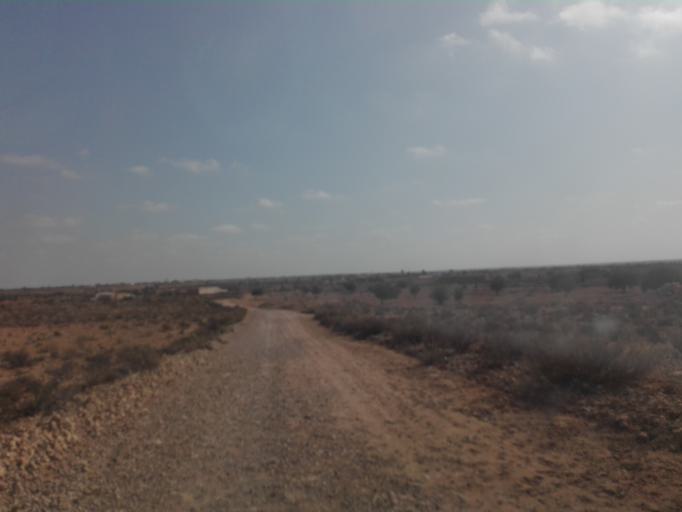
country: TN
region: Madanin
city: Medenine
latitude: 33.4323
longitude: 10.4156
